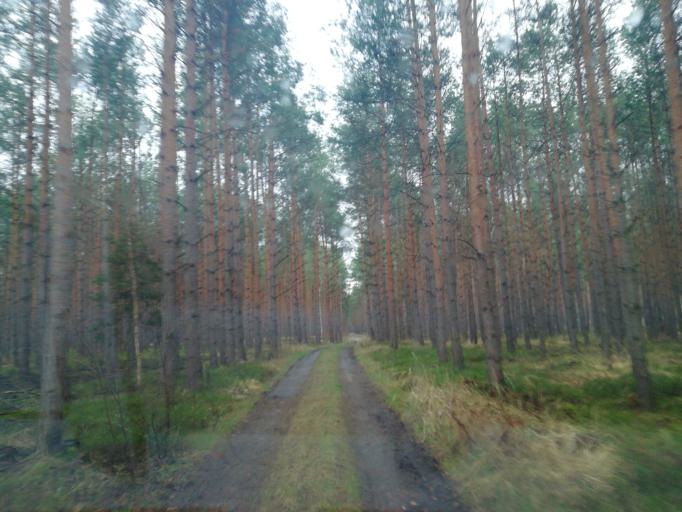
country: DE
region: Brandenburg
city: Schonborn
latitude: 51.6670
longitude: 13.4890
